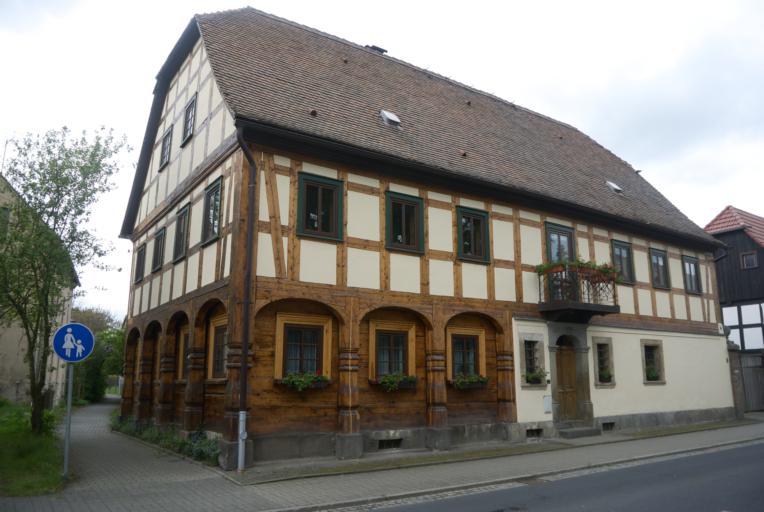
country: DE
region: Saxony
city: Hirschfelde
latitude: 50.9463
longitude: 14.8893
